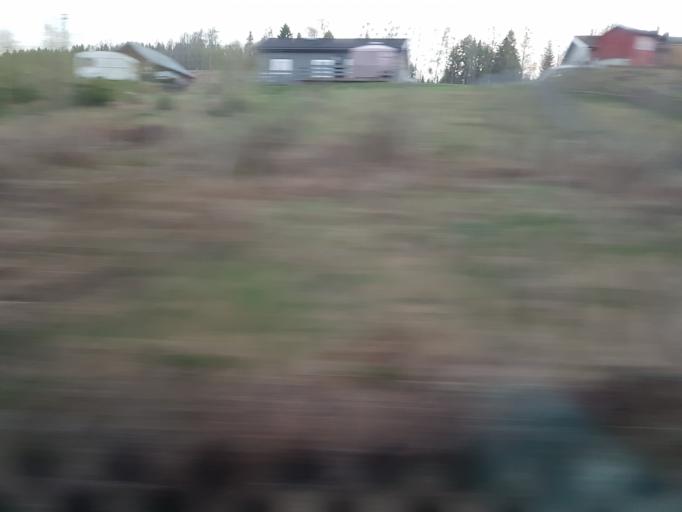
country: NO
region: Hedmark
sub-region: Ringsaker
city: Moelv
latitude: 60.9137
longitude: 10.7523
